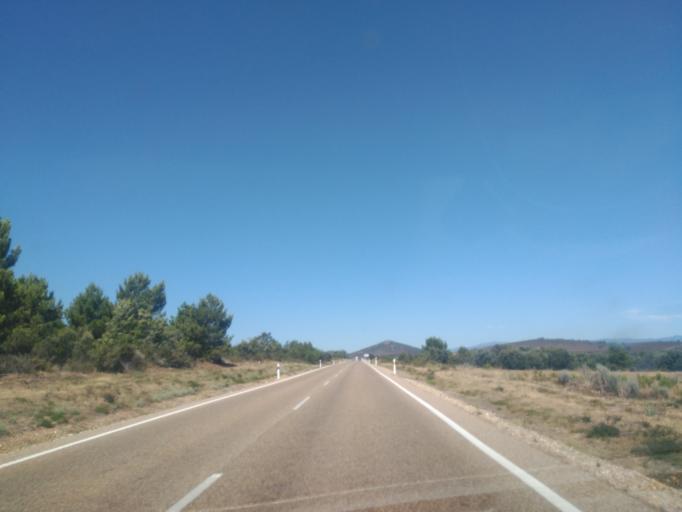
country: ES
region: Castille and Leon
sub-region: Provincia de Zamora
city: Otero de Bodas
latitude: 41.9281
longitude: -6.1097
